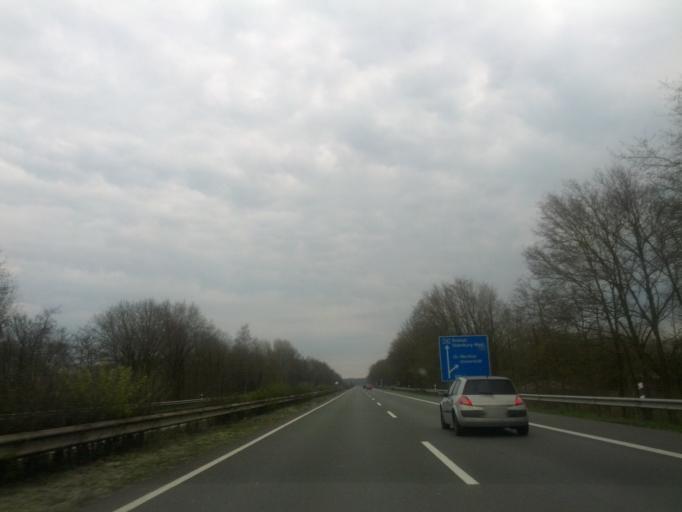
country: DE
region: Lower Saxony
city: Oldenburg
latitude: 53.1590
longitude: 8.1523
